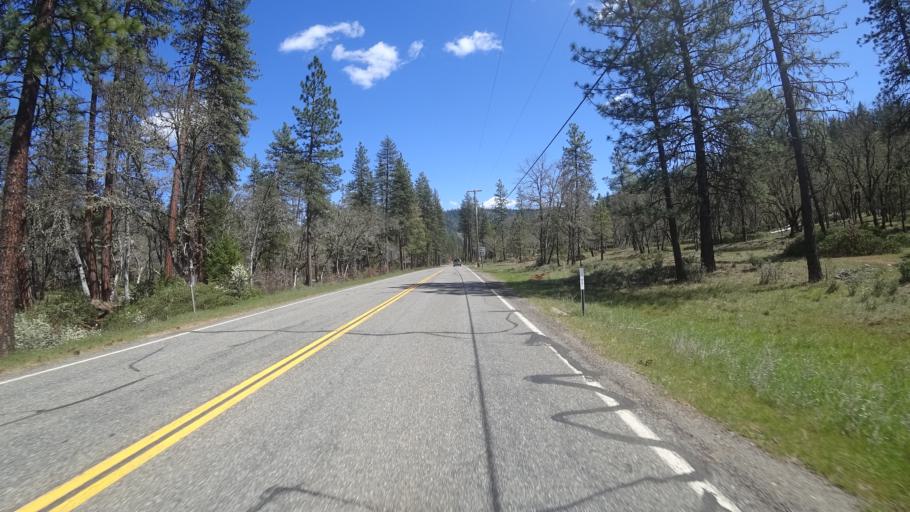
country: US
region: California
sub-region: Trinity County
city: Weaverville
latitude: 40.7533
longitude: -122.9057
